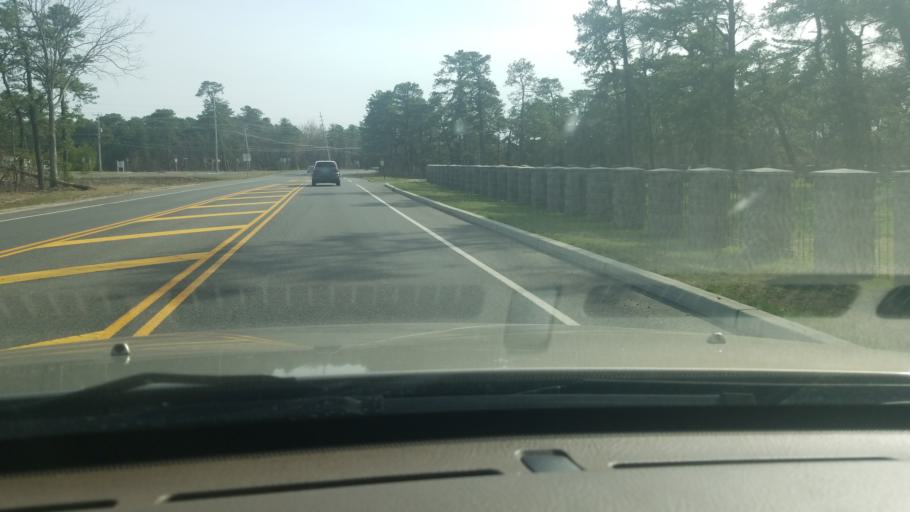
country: US
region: New Jersey
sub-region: Ocean County
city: Lakehurst
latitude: 40.0180
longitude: -74.3099
